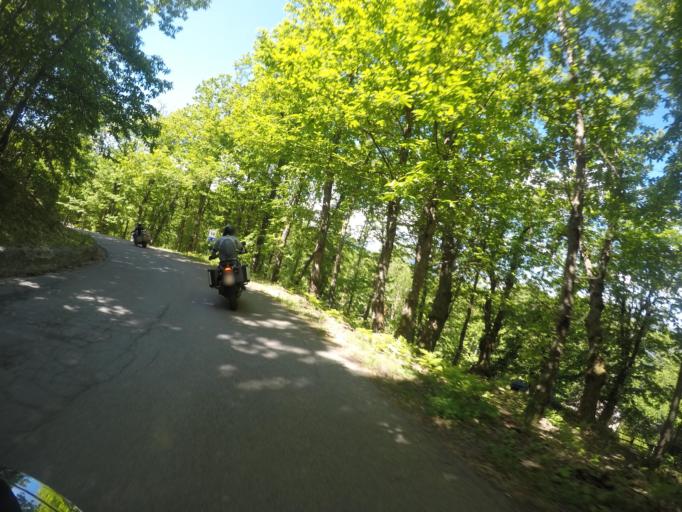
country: IT
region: Tuscany
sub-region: Provincia di Lucca
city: Careggine
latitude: 44.1126
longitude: 10.3293
